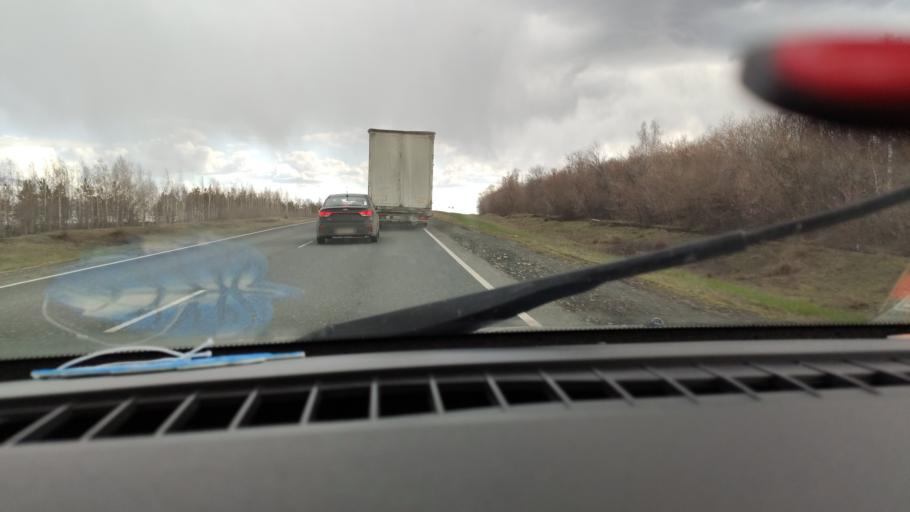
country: RU
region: Saratov
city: Balakovo
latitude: 52.1622
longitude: 47.8232
